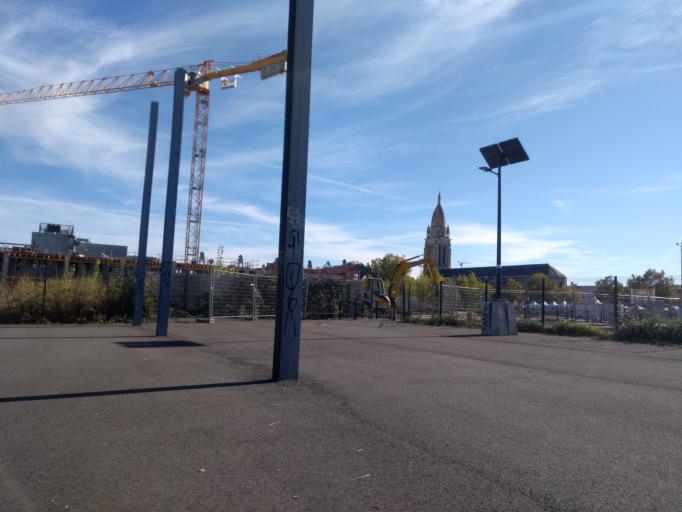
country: FR
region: Aquitaine
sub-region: Departement de la Gironde
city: Bordeaux
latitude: 44.8450
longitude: -0.5566
